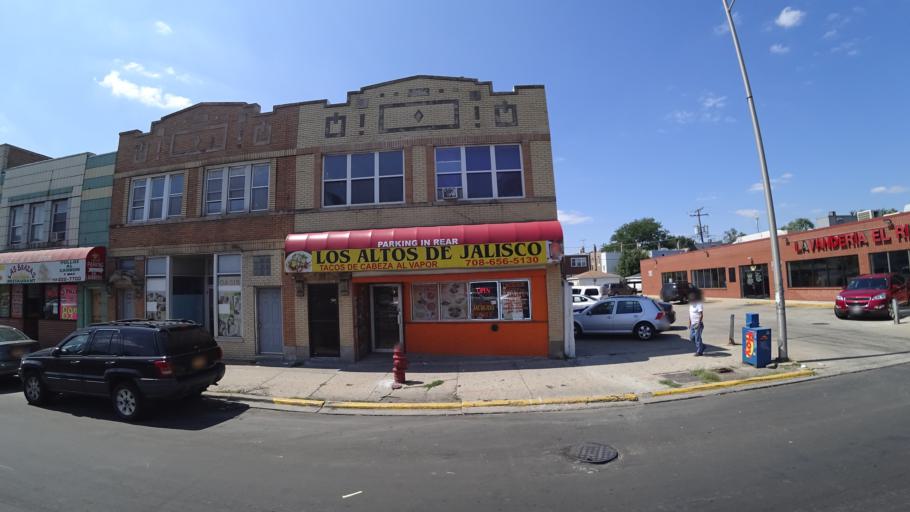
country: US
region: Illinois
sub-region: Cook County
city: Cicero
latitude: 41.8541
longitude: -87.7444
